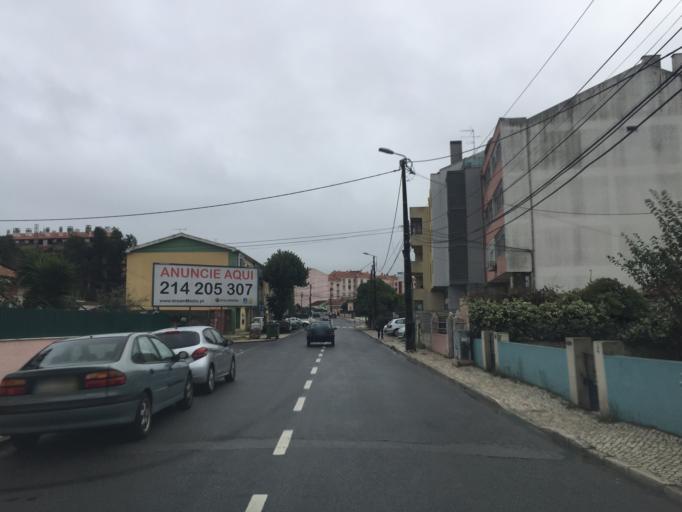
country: PT
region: Lisbon
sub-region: Sintra
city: Rio de Mouro
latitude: 38.7907
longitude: -9.3463
